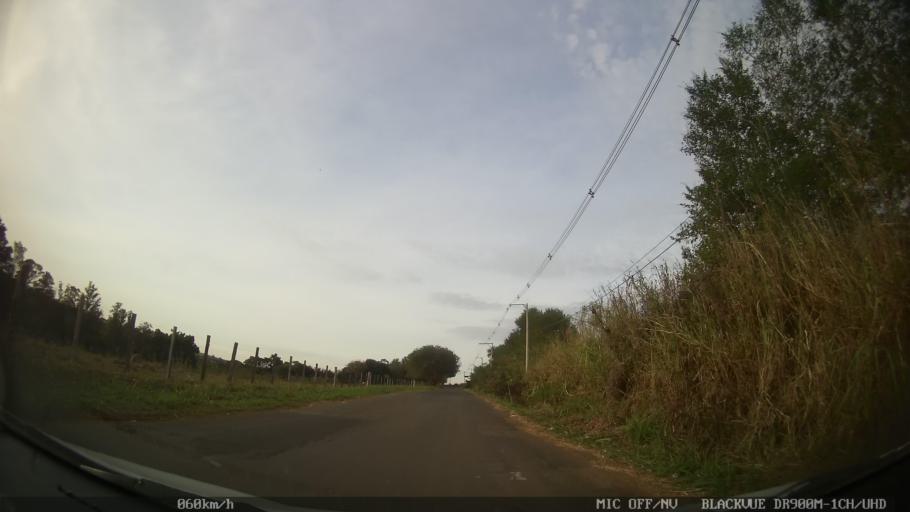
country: BR
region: Sao Paulo
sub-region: Piracicaba
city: Piracicaba
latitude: -22.6950
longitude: -47.5849
